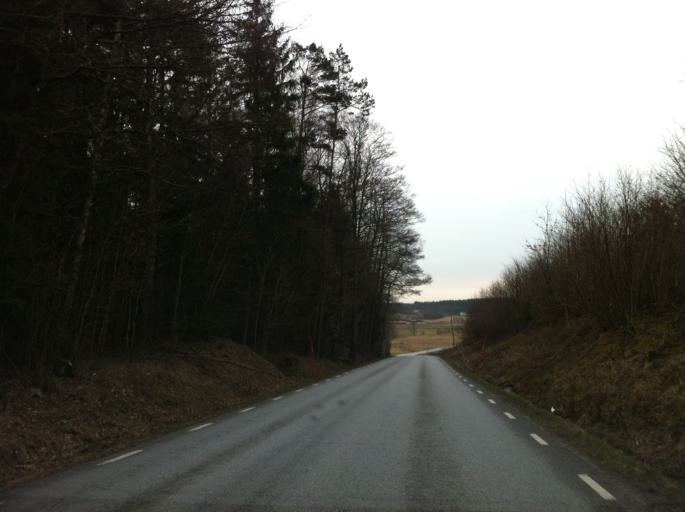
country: SE
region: Vaestra Goetaland
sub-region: Orust
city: Henan
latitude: 58.2454
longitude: 11.6853
